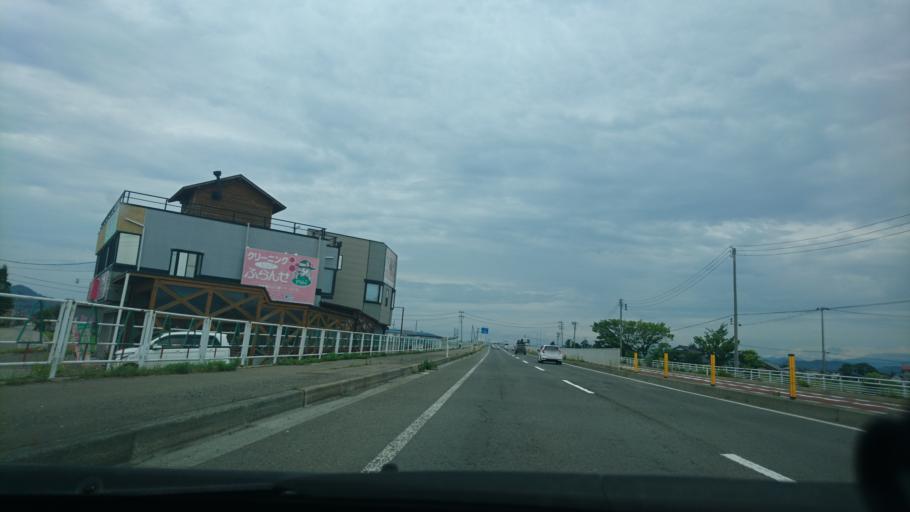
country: JP
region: Akita
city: Omagari
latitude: 39.4583
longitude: 140.4955
